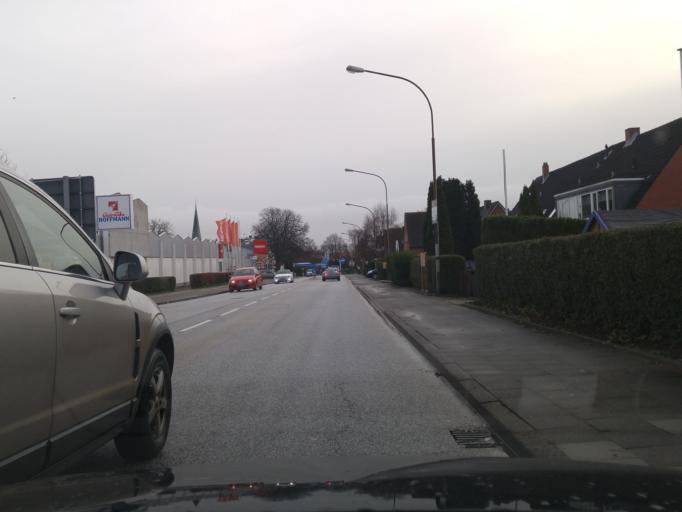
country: DE
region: Schleswig-Holstein
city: Travemuende
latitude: 53.9615
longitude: 10.8603
